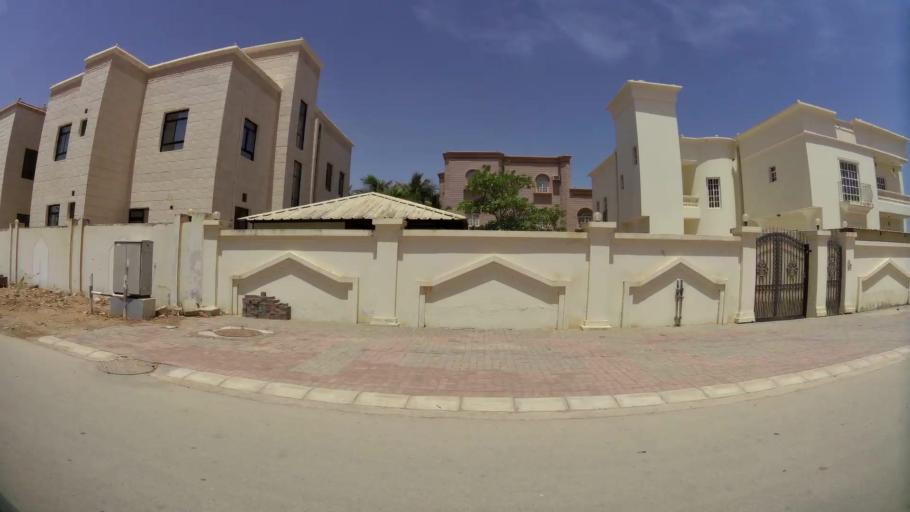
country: OM
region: Zufar
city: Salalah
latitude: 17.0643
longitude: 54.1509
